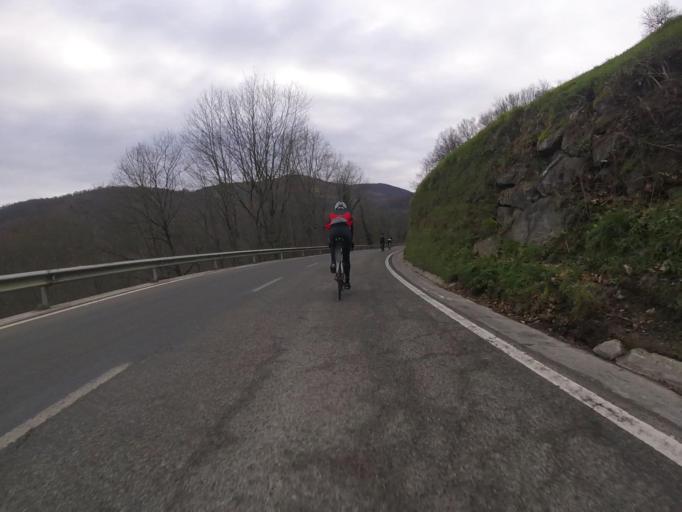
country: ES
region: Navarre
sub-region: Provincia de Navarra
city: Igantzi
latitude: 43.2217
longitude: -1.6962
